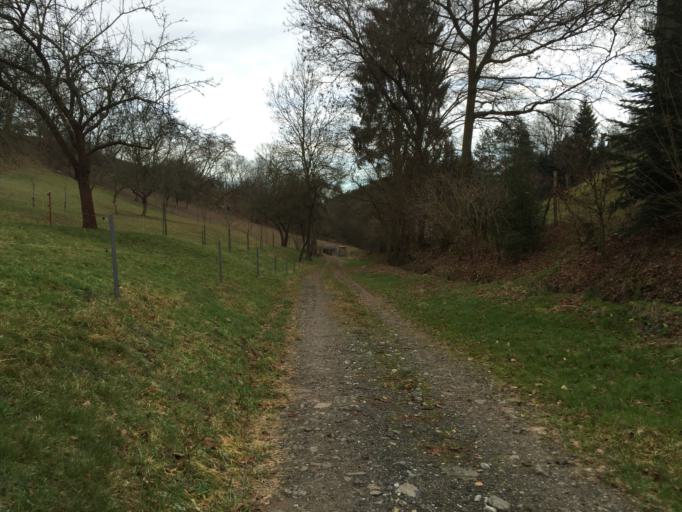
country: DE
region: Thuringia
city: Orlamunde
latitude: 50.7763
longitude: 11.5204
